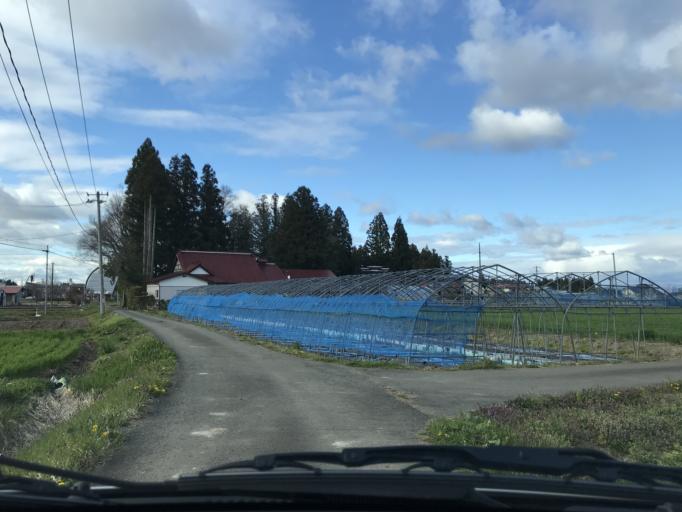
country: JP
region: Iwate
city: Mizusawa
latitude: 39.1041
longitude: 141.1230
